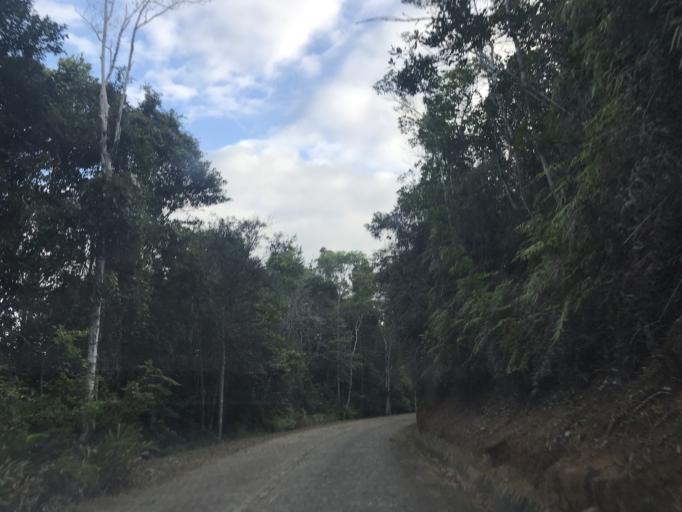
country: BR
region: Bahia
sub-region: Gandu
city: Gandu
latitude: -13.9104
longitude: -39.4612
